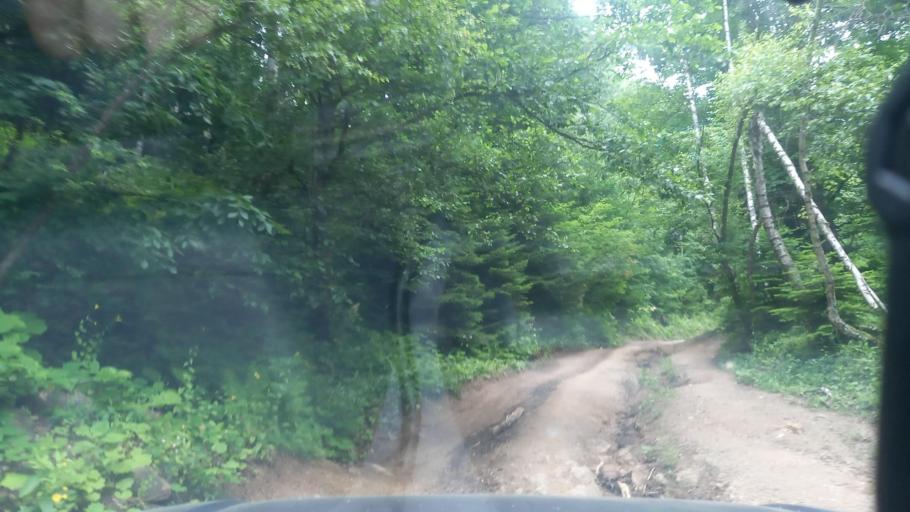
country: RU
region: Karachayevo-Cherkesiya
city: Kurdzhinovo
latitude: 43.8056
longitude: 40.8594
